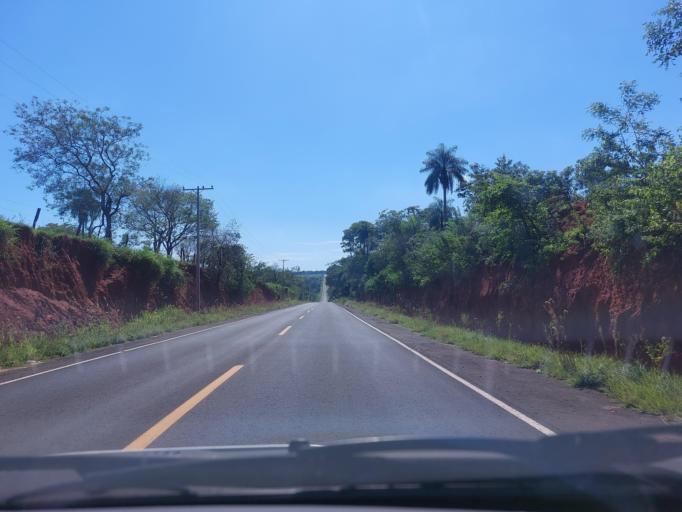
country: PY
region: San Pedro
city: Guayaybi
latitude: -24.5552
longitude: -56.5196
